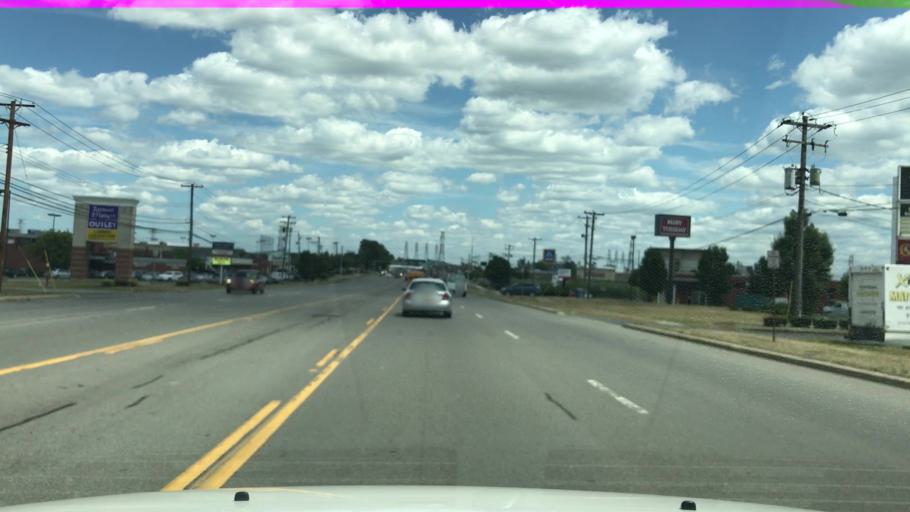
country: US
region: New York
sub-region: Erie County
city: Sloan
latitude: 42.9073
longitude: -78.7772
